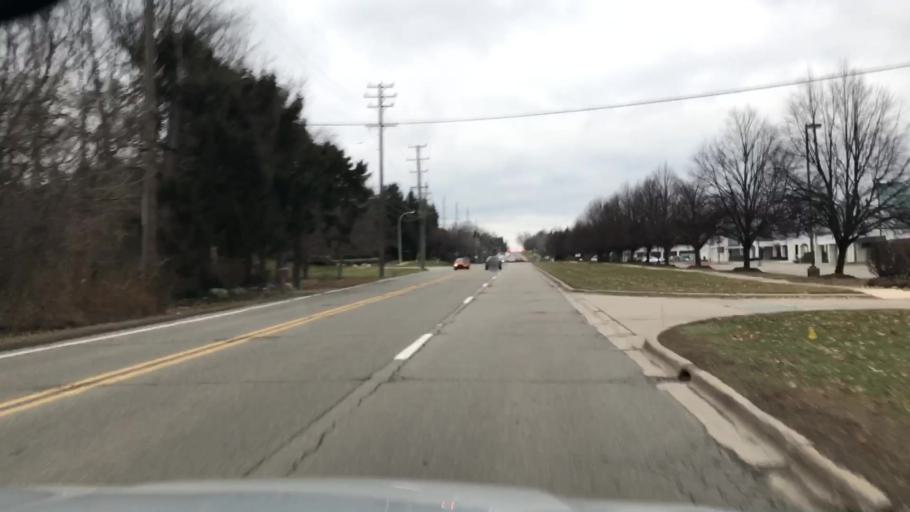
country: US
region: Michigan
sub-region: Wayne County
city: Northville
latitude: 42.4485
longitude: -83.4738
